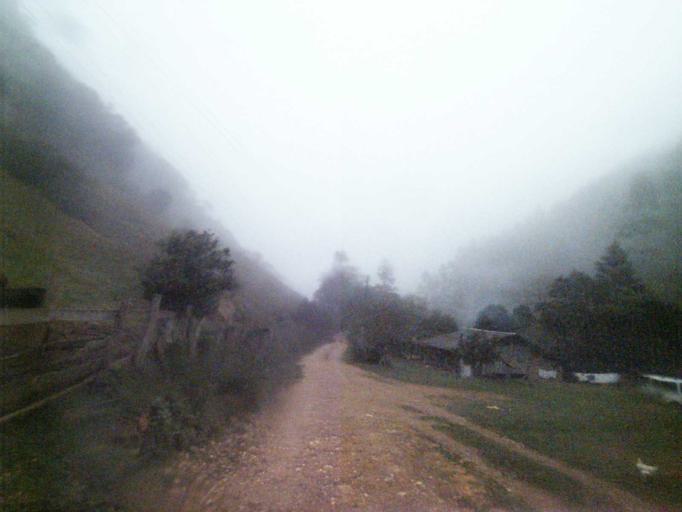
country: BR
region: Santa Catarina
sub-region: Anitapolis
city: Anitapolis
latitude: -27.7889
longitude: -49.1374
